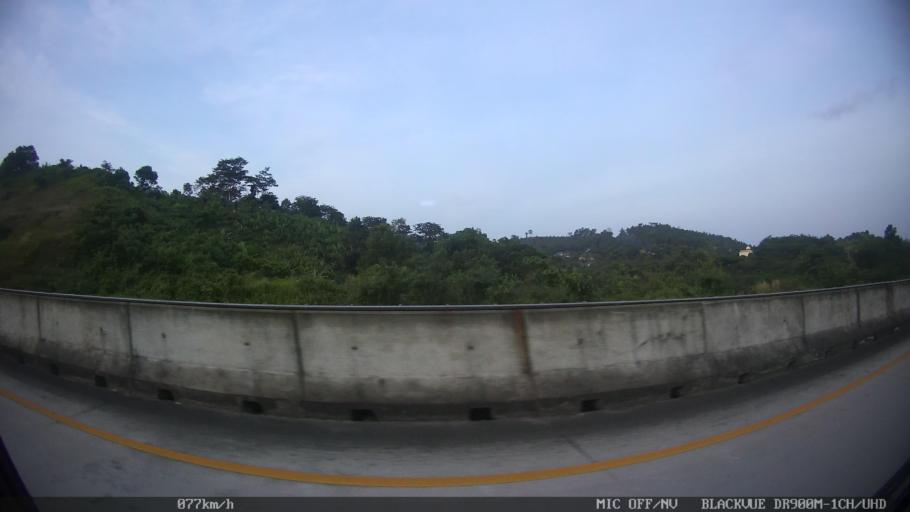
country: ID
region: Lampung
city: Penengahan
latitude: -5.8581
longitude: 105.7313
